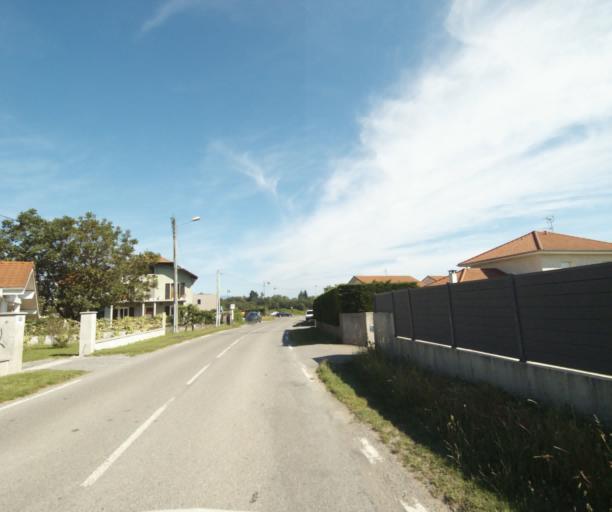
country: FR
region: Rhone-Alpes
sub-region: Departement de la Haute-Savoie
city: Thonon-les-Bains
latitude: 46.3862
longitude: 6.5023
